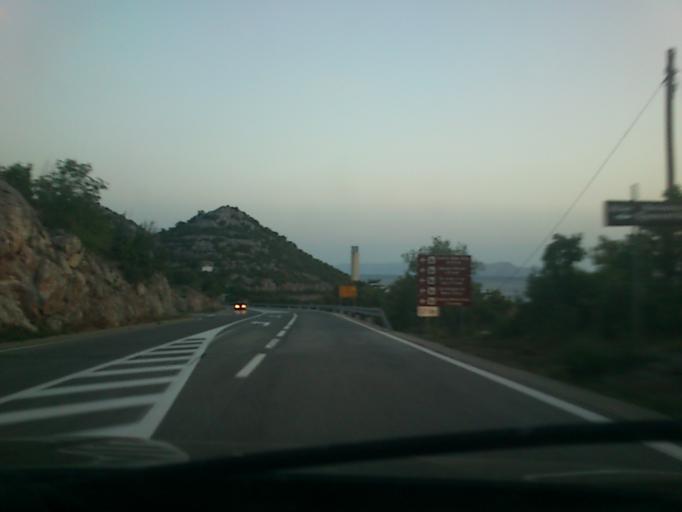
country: HR
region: Licko-Senjska
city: Senj
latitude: 44.9251
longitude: 14.9173
